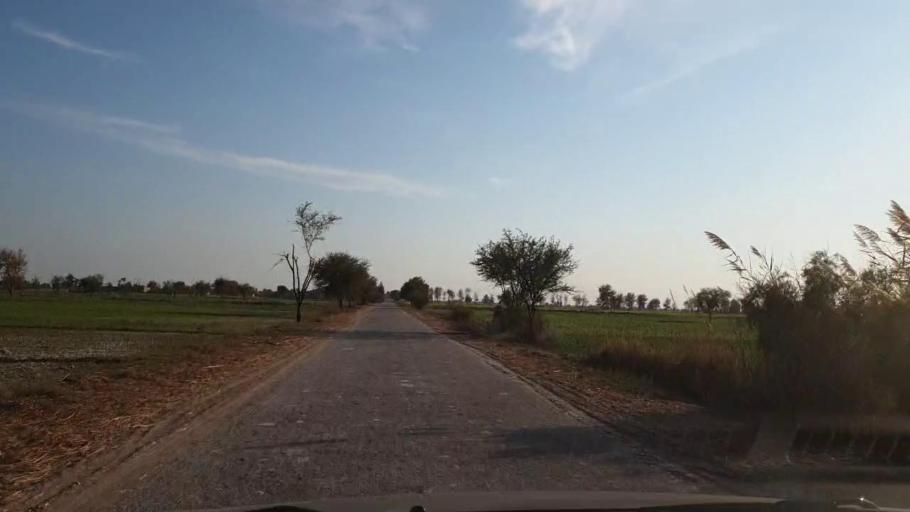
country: PK
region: Sindh
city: Khadro
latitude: 26.1959
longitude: 68.7468
